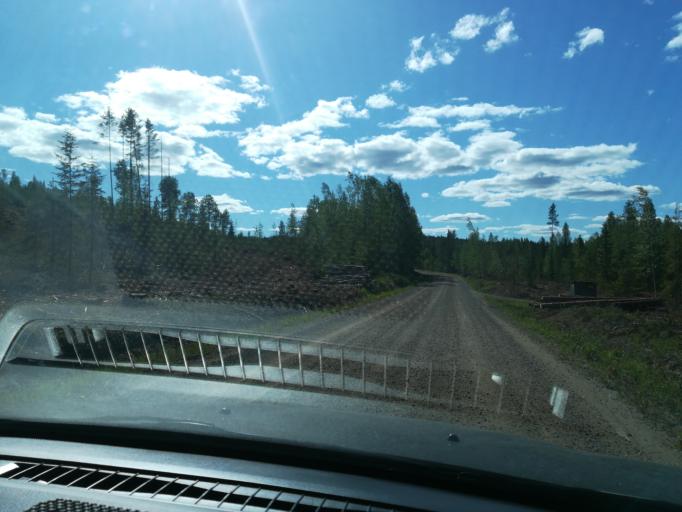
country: FI
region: Southern Savonia
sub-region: Mikkeli
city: Puumala
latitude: 61.6563
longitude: 28.1193
